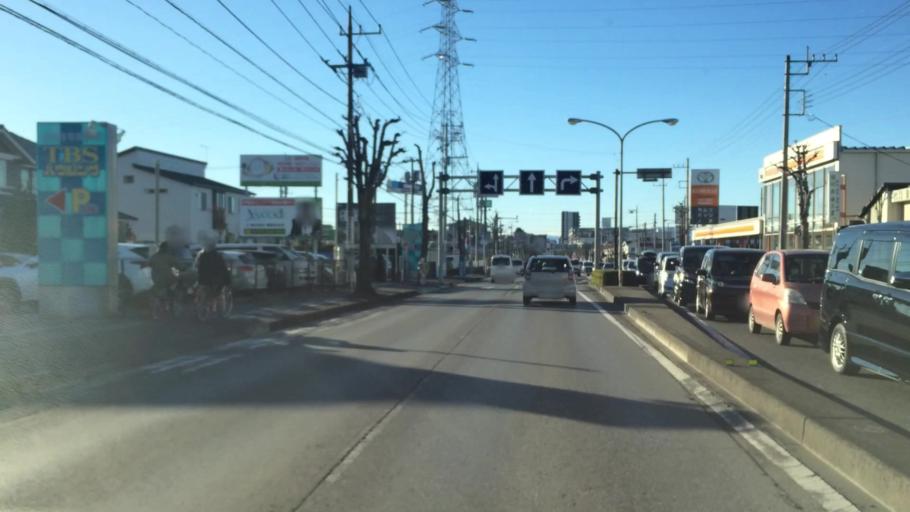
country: JP
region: Tochigi
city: Utsunomiya-shi
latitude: 36.5571
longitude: 139.9283
